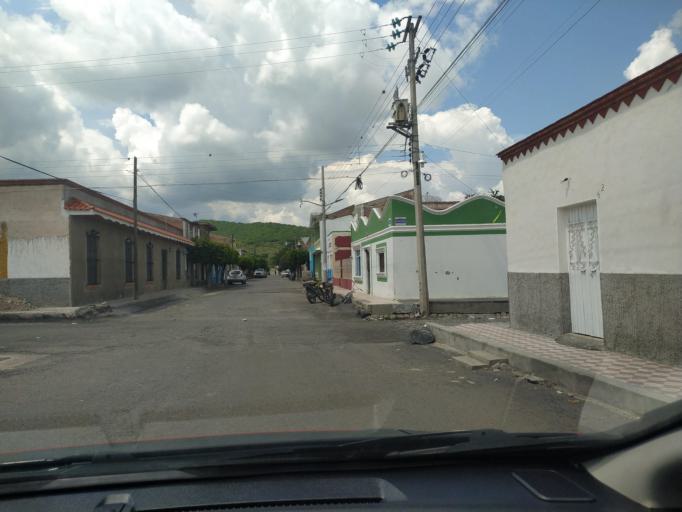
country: MX
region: Jalisco
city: Villa Corona
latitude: 20.3492
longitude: -103.6697
